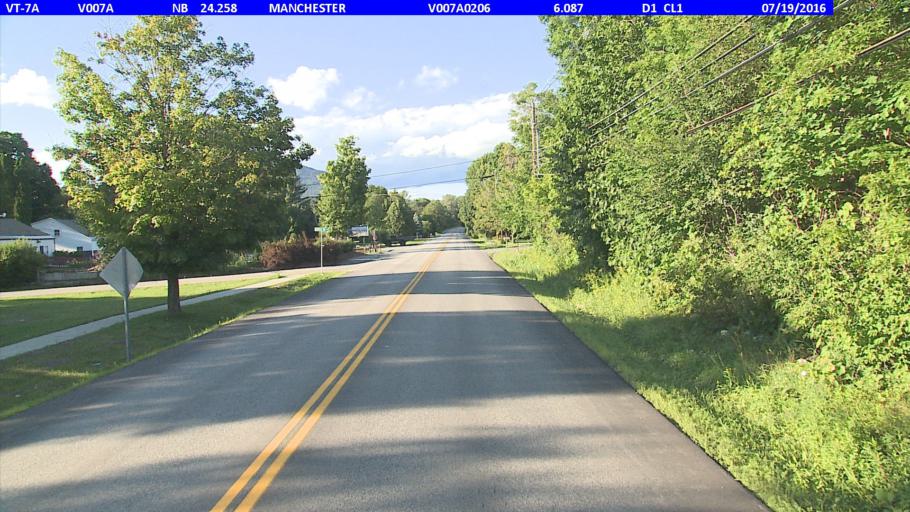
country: US
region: Vermont
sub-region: Bennington County
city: Manchester Center
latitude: 43.1892
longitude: -73.0428
